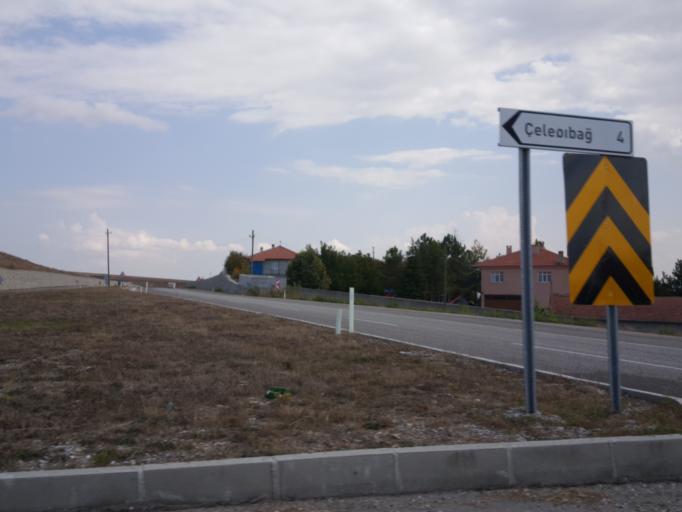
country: TR
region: Corum
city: Alaca
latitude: 40.1571
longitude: 34.7096
